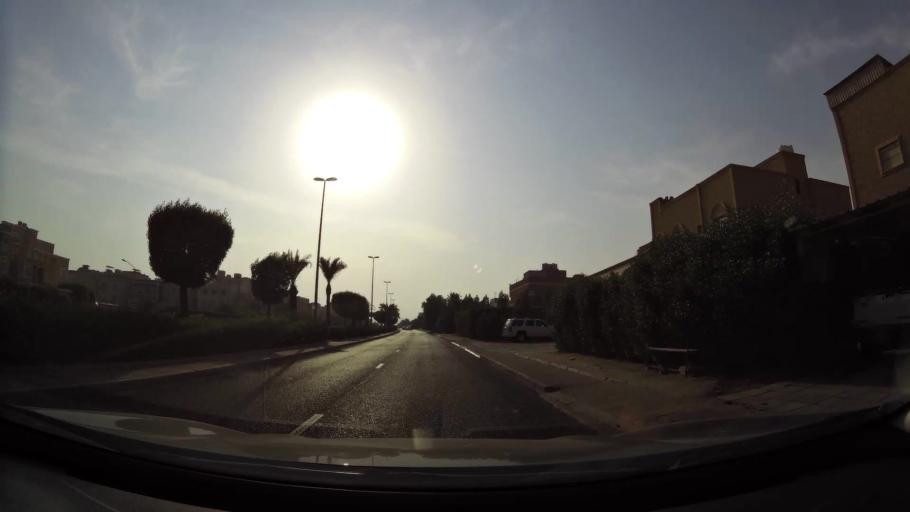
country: KW
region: Mubarak al Kabir
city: Mubarak al Kabir
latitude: 29.1965
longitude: 48.0752
